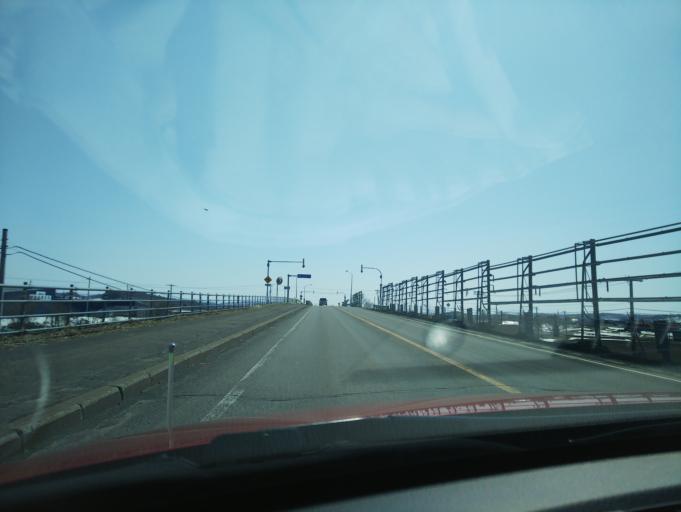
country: JP
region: Hokkaido
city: Nayoro
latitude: 44.1974
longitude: 142.3950
